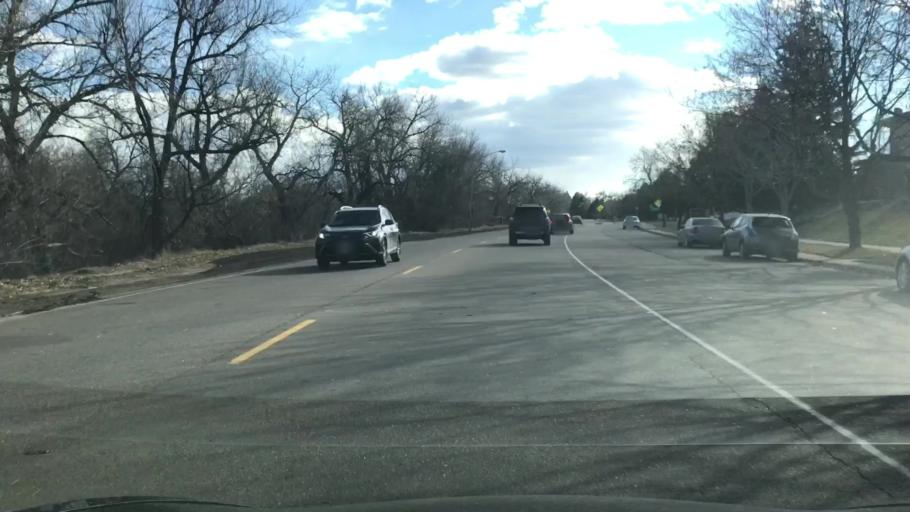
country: US
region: Colorado
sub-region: Arapahoe County
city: Glendale
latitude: 39.7016
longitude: -104.9283
